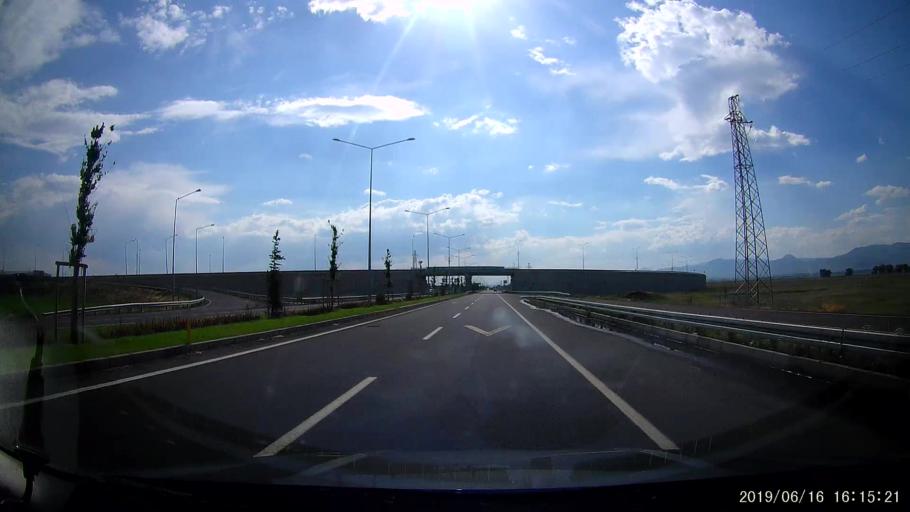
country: TR
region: Erzurum
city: Erzurum
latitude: 39.9618
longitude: 41.2281
